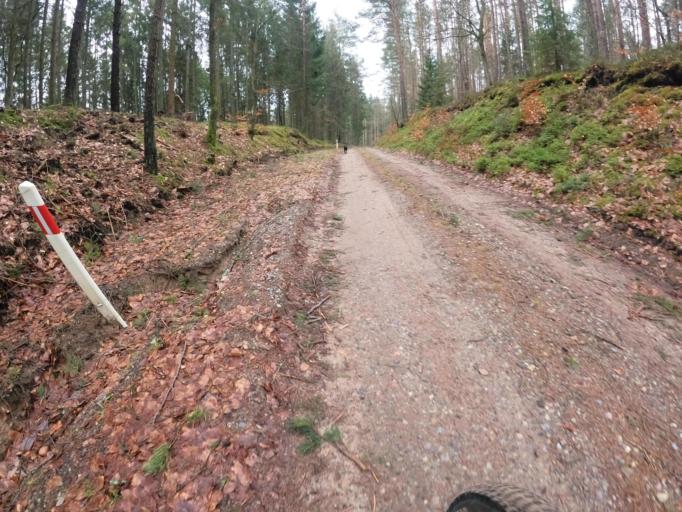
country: PL
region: West Pomeranian Voivodeship
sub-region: Powiat koszalinski
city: Polanow
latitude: 54.2290
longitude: 16.6848
